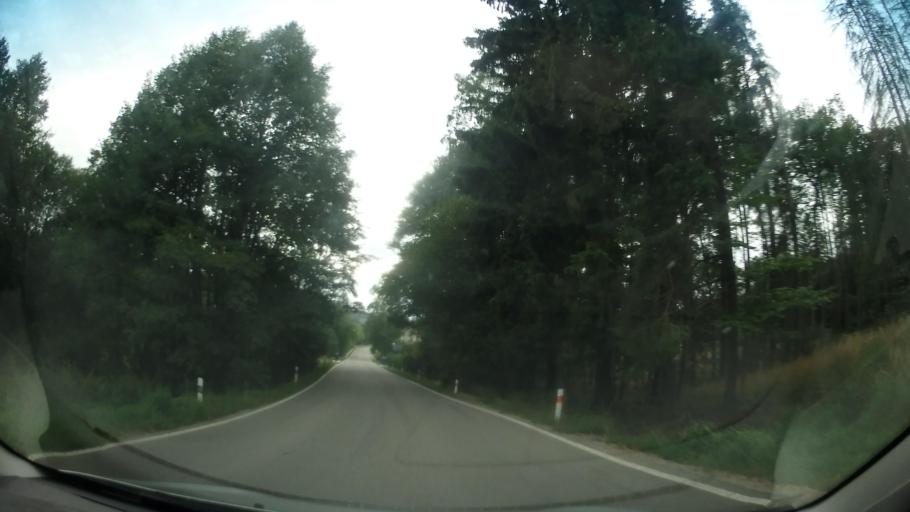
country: CZ
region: Pardubicky
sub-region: Okres Chrudim
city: Nasavrky
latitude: 49.8040
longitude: 15.7527
